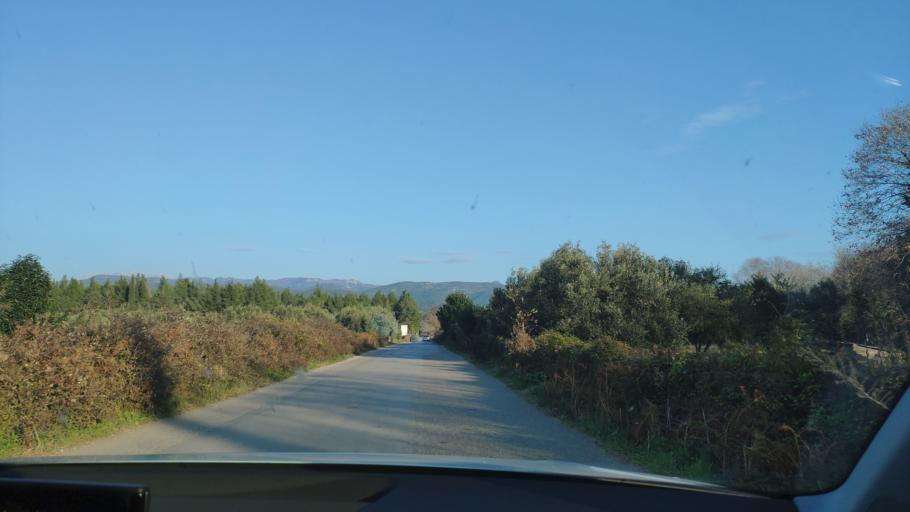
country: GR
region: West Greece
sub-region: Nomos Aitolias kai Akarnanias
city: Krikellos
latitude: 38.9306
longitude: 21.1665
